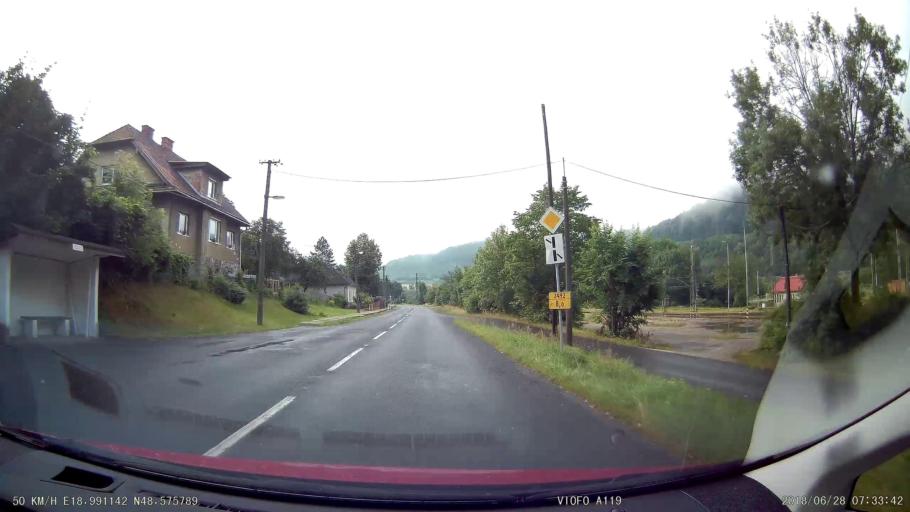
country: SK
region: Banskobystricky
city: Ziar nad Hronom
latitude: 48.5757
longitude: 18.9912
